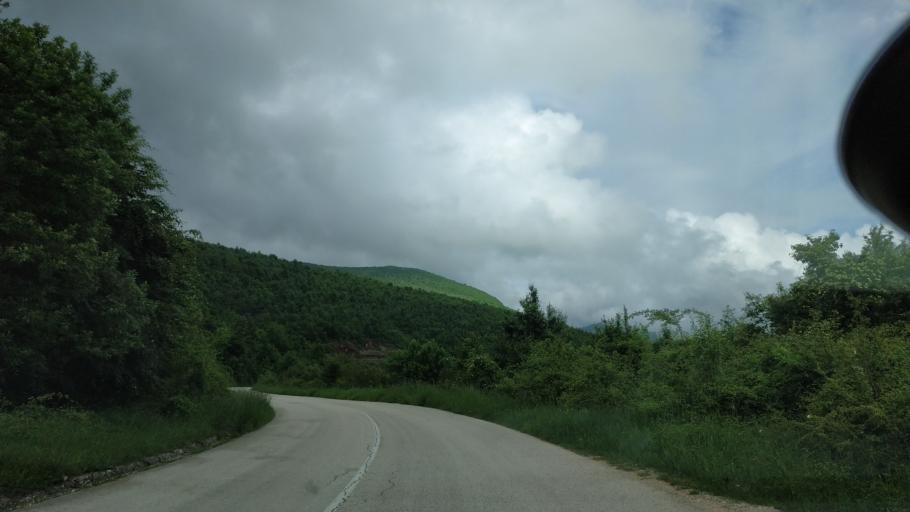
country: RS
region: Central Serbia
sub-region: Zajecarski Okrug
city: Boljevac
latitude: 43.7271
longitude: 21.9523
